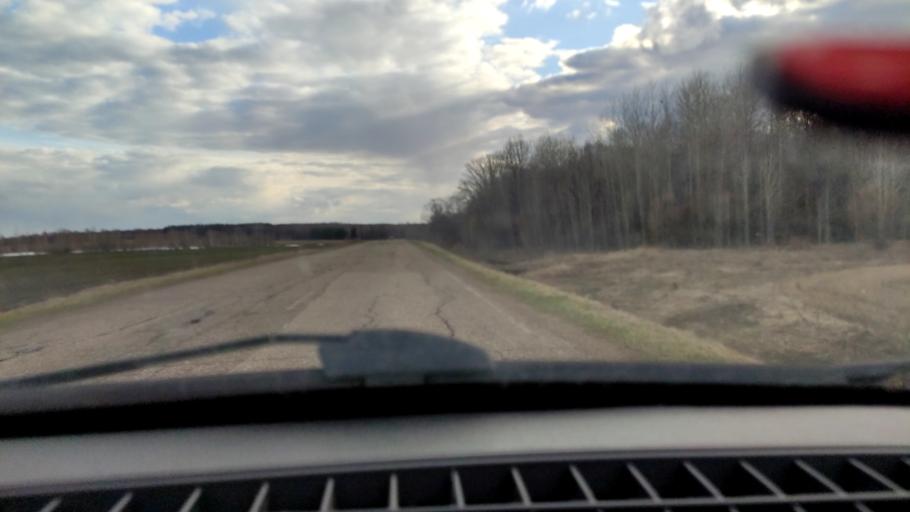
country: RU
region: Bashkortostan
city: Karmaskaly
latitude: 54.3239
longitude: 55.9855
